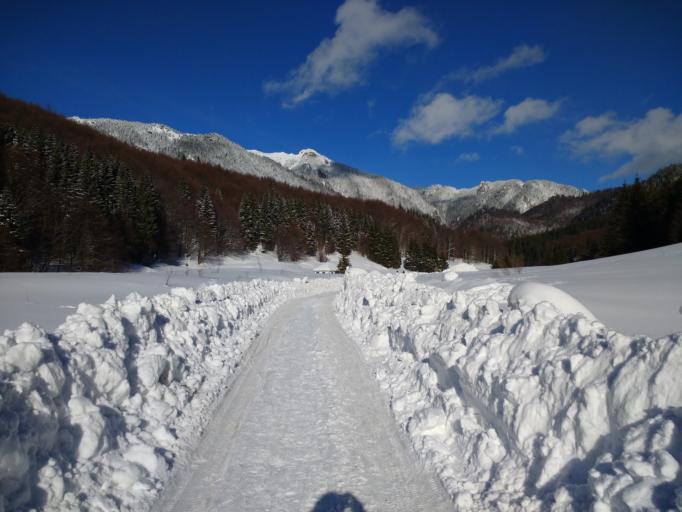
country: RO
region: Brasov
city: Crivina
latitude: 45.4839
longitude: 25.9205
